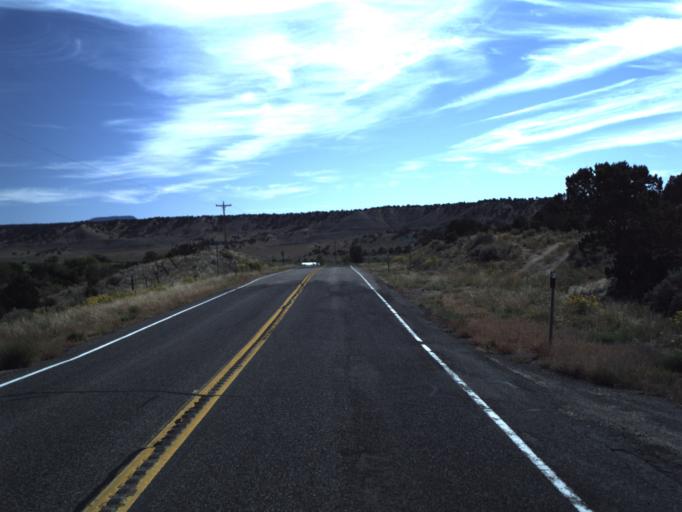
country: US
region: Utah
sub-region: Garfield County
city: Panguitch
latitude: 37.6128
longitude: -112.0664
